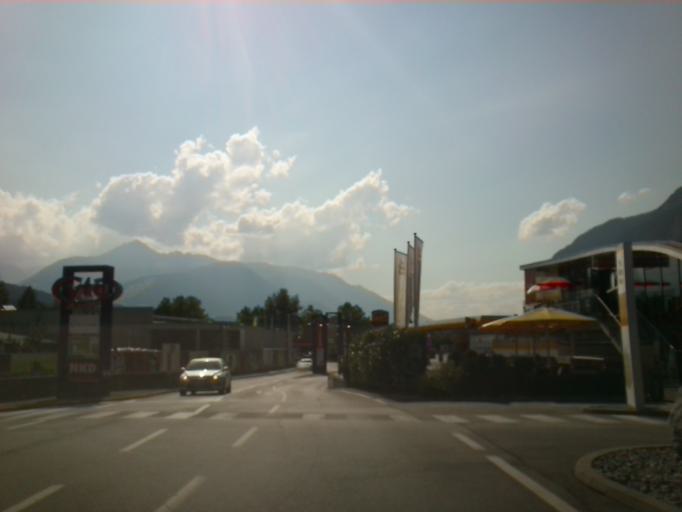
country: AT
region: Tyrol
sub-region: Politischer Bezirk Innsbruck Land
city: Vols
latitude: 47.2573
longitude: 11.3253
